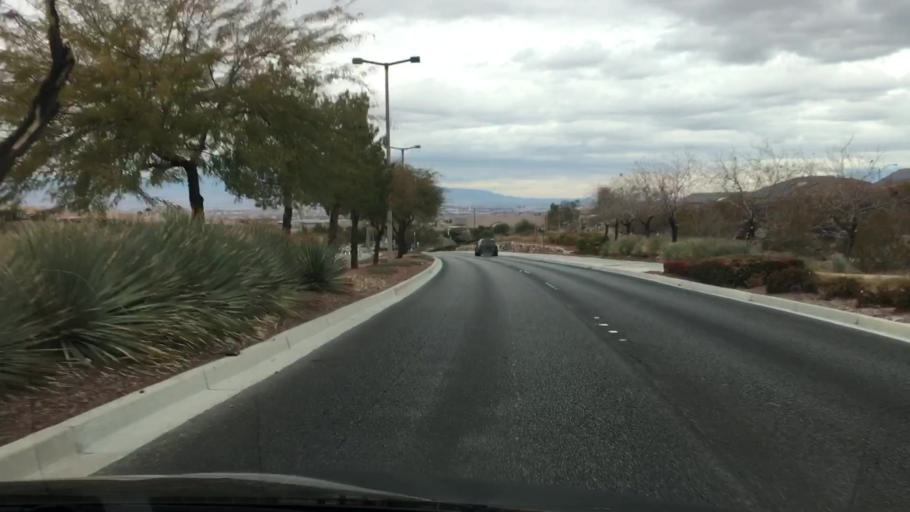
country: US
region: Nevada
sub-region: Clark County
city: Whitney
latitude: 35.9565
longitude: -115.1153
